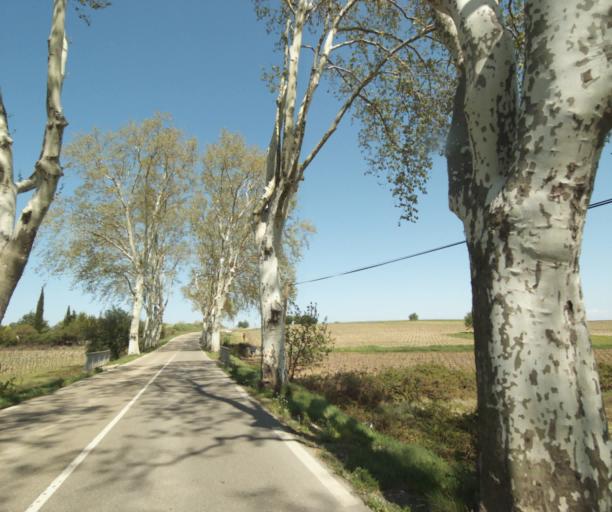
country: FR
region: Languedoc-Roussillon
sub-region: Departement de l'Herault
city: Restinclieres
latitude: 43.7288
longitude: 4.0431
